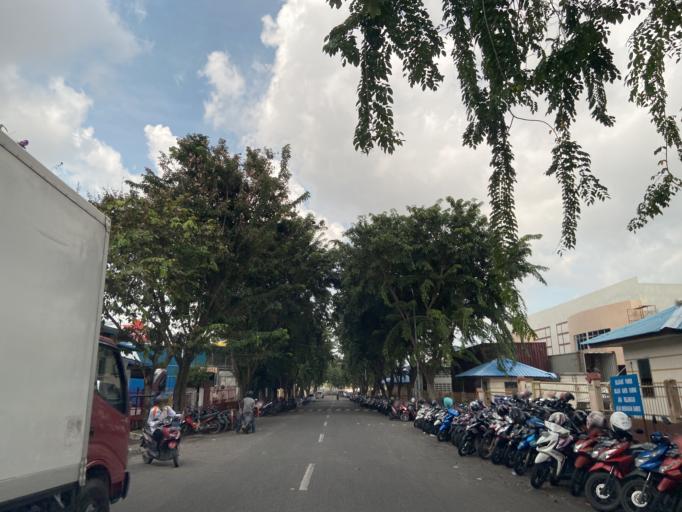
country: SG
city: Singapore
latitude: 1.1074
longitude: 104.0711
